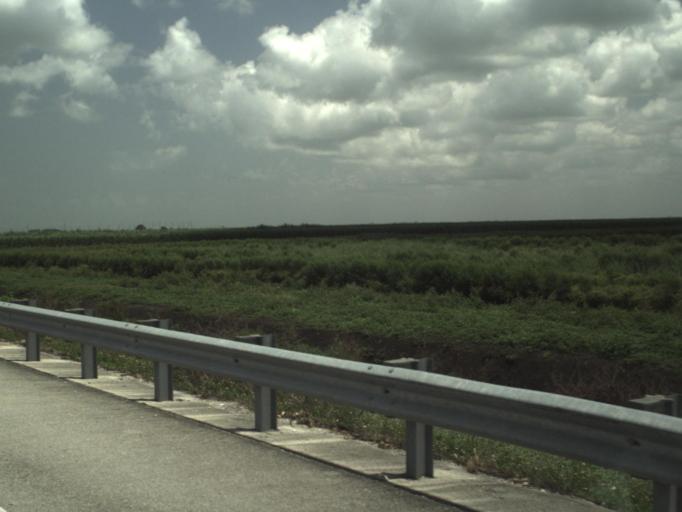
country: US
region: Florida
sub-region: Palm Beach County
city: Pahokee
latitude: 26.7606
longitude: -80.6597
